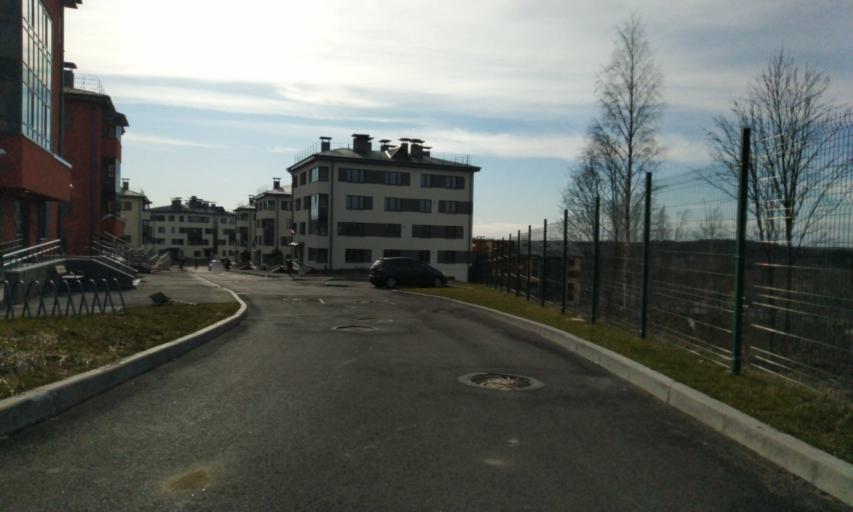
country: RU
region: Leningrad
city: Bugry
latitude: 60.1228
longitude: 30.4250
